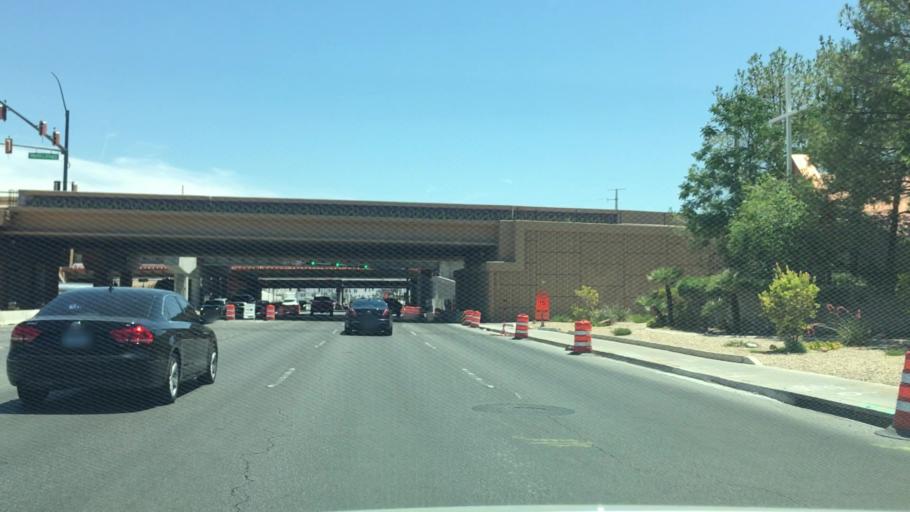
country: US
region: Nevada
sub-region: Clark County
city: Las Vegas
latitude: 36.1588
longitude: -115.1625
